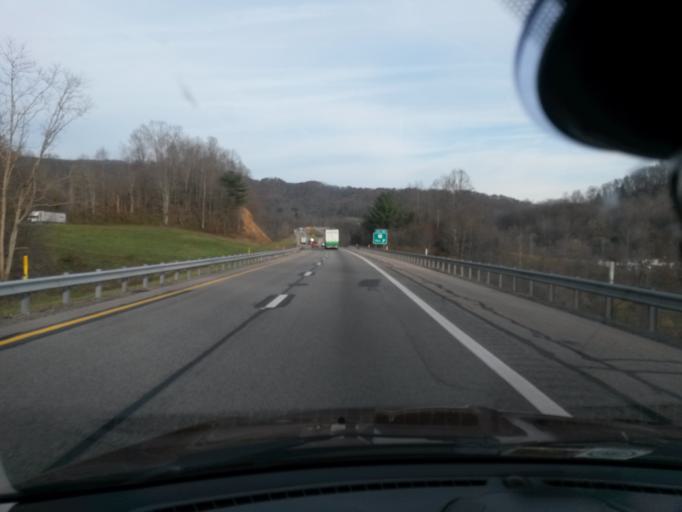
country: US
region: West Virginia
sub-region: Raleigh County
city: Bradley
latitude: 37.9110
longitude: -81.2671
